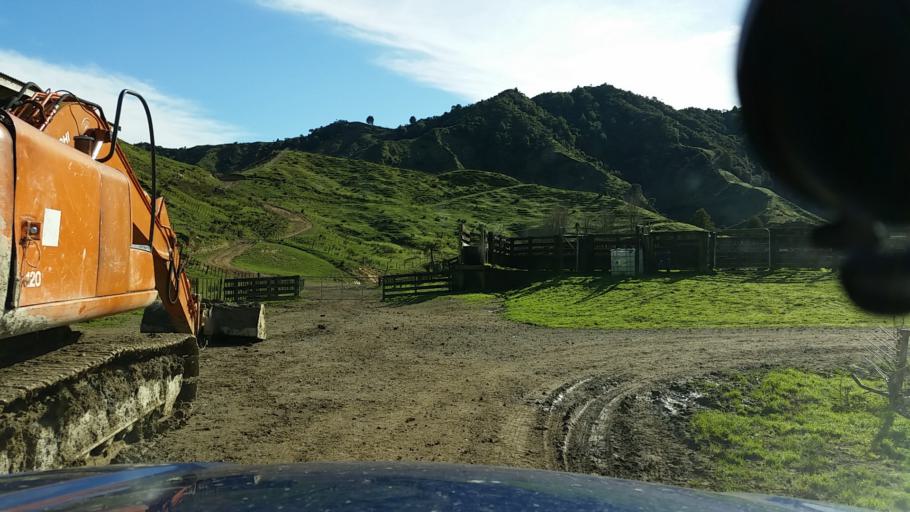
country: NZ
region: Taranaki
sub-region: New Plymouth District
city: Waitara
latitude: -39.0512
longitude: 174.7471
